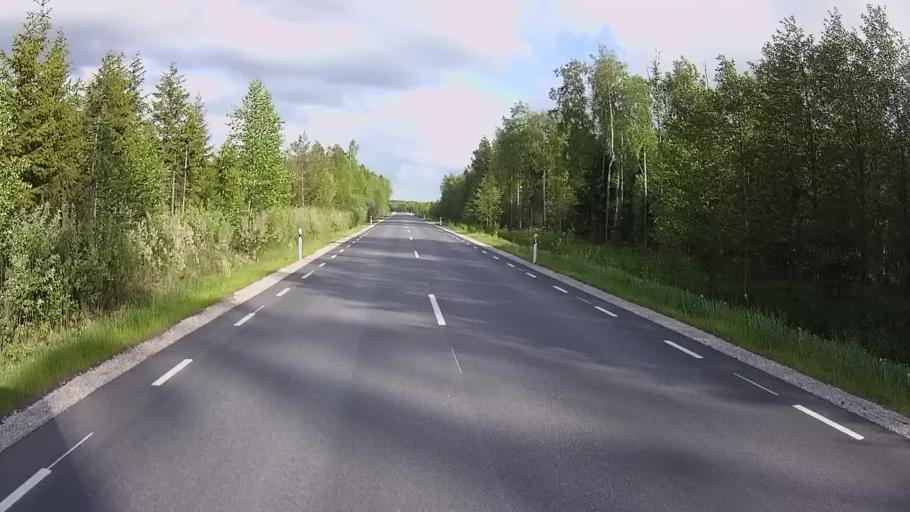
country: EE
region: Ida-Virumaa
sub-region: Kivioli linn
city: Kivioli
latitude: 59.2037
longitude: 26.8121
